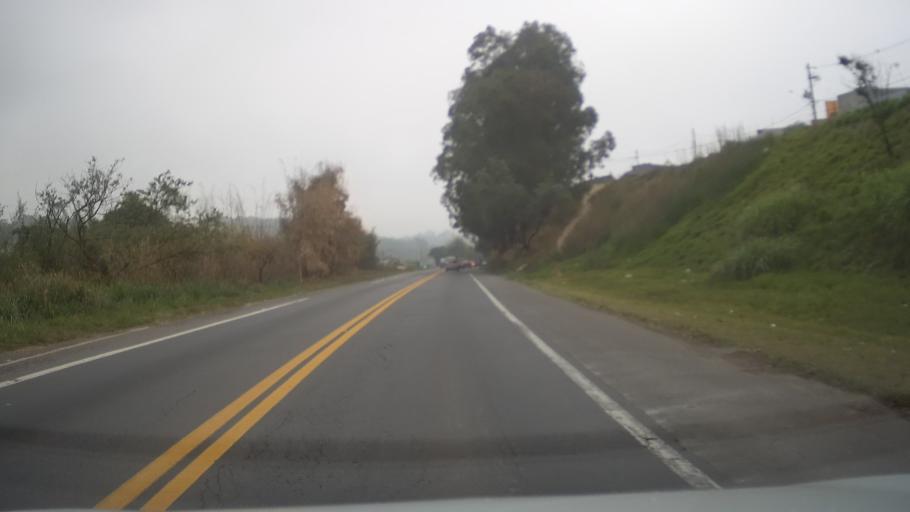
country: BR
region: Sao Paulo
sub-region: Itatiba
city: Itatiba
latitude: -23.0050
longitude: -46.8173
